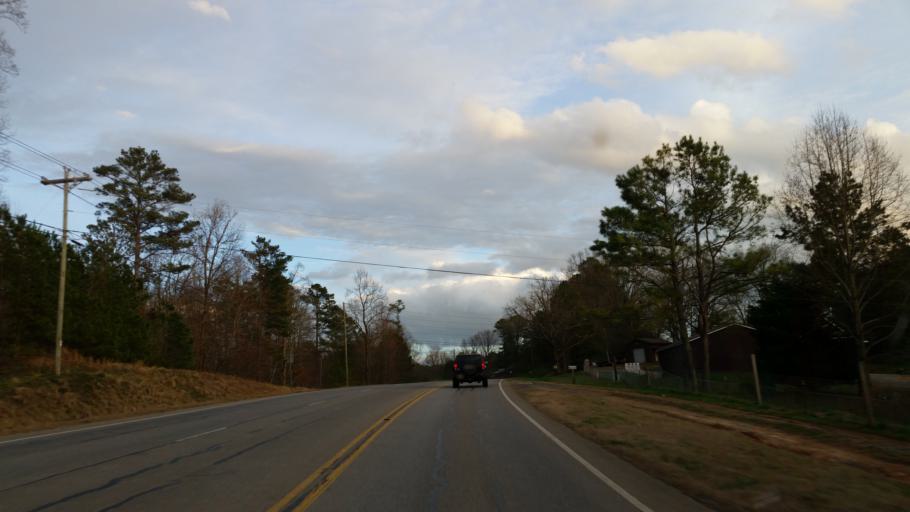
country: US
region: Georgia
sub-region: Pickens County
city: Jasper
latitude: 34.4787
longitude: -84.5395
